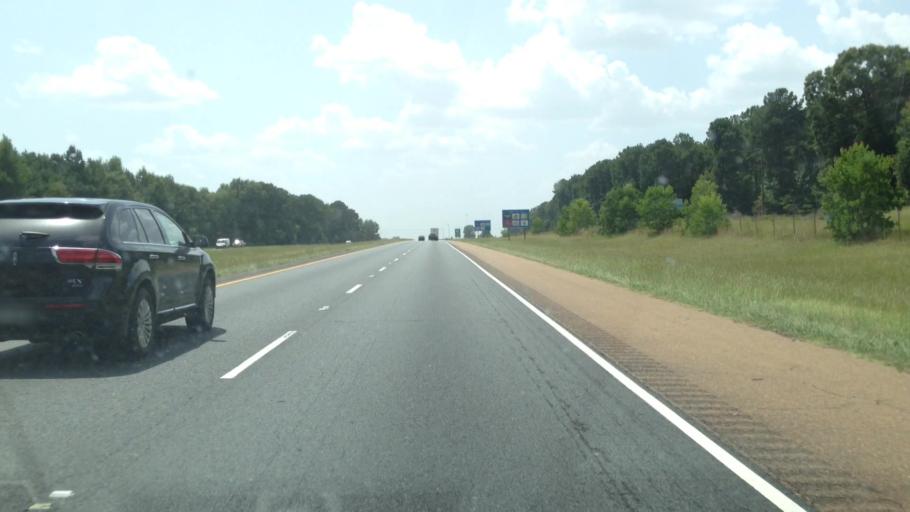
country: US
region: Louisiana
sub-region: Bienville Parish
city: Arcadia
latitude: 32.5614
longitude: -92.8997
